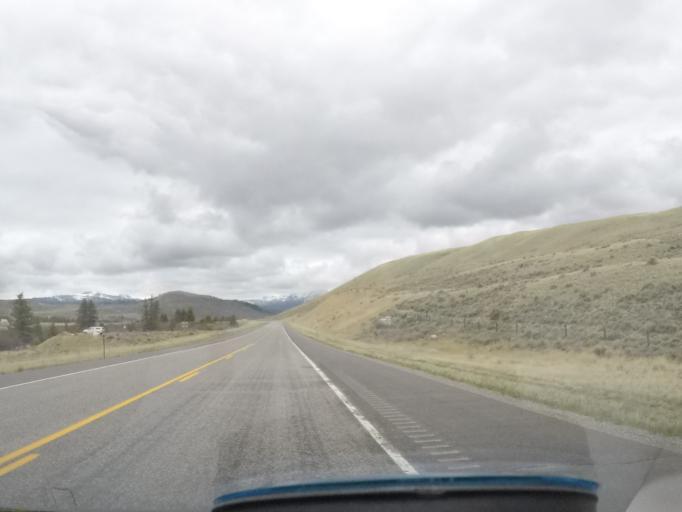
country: US
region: Wyoming
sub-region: Sublette County
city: Pinedale
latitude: 43.5908
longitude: -109.7737
